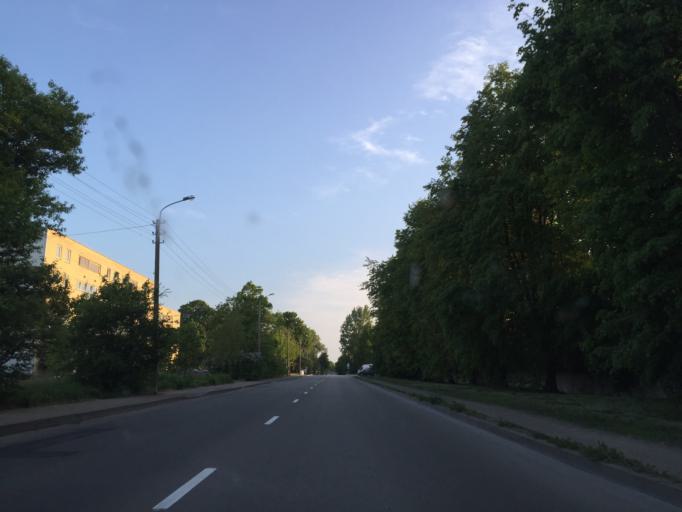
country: LT
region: Siauliu apskritis
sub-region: Siauliai
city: Siauliai
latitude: 55.9521
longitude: 23.3265
